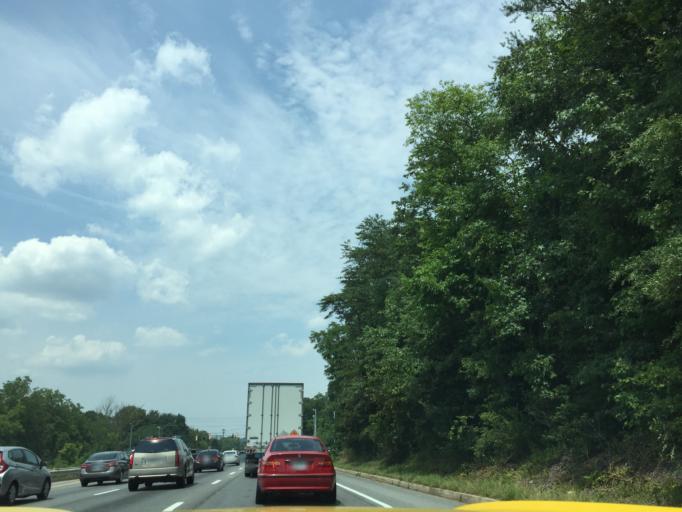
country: US
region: Maryland
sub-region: Prince George's County
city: Friendly
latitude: 38.7543
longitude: -76.9929
